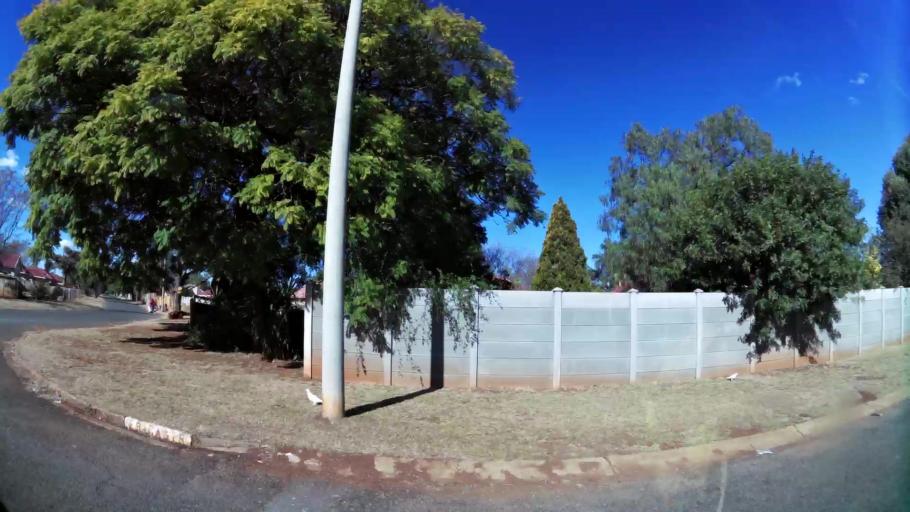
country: ZA
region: Gauteng
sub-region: West Rand District Municipality
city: Carletonville
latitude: -26.3726
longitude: 27.3992
